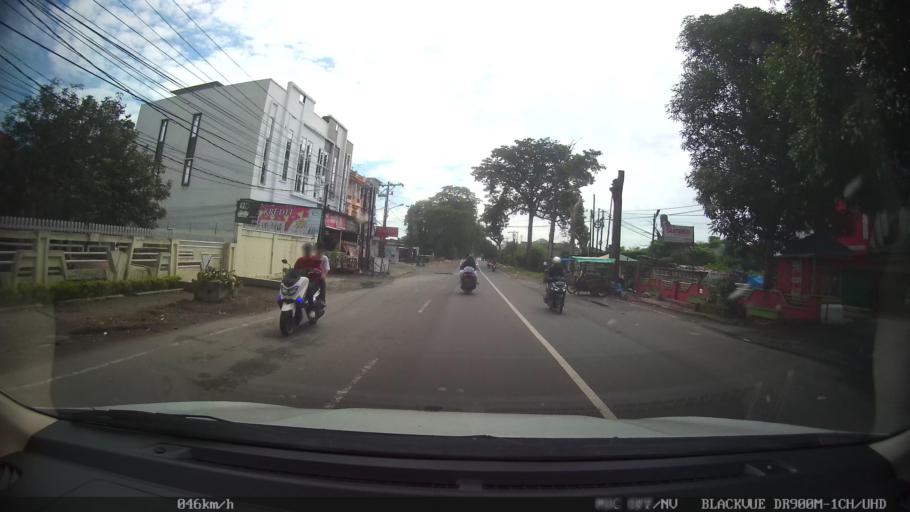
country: ID
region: North Sumatra
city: Medan
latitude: 3.6225
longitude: 98.6922
